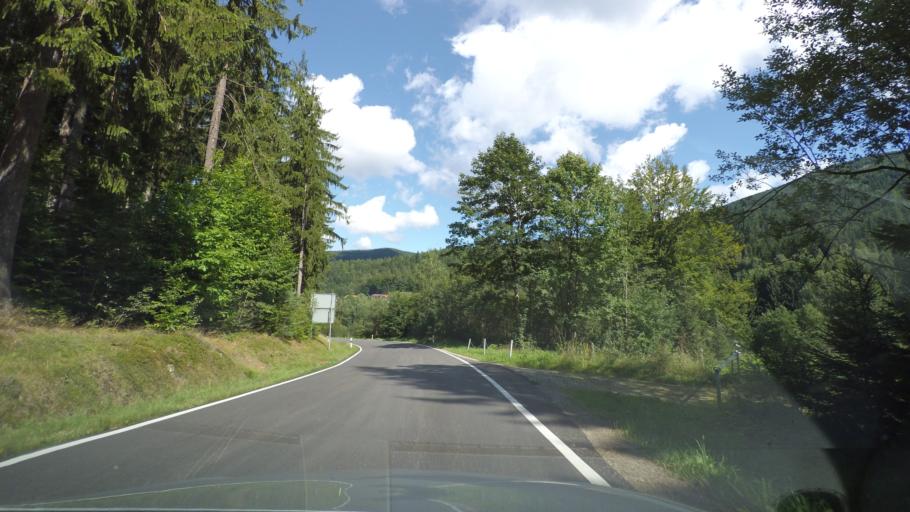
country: DE
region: Bavaria
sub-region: Lower Bavaria
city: Bodenmais
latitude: 49.0650
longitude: 13.1174
